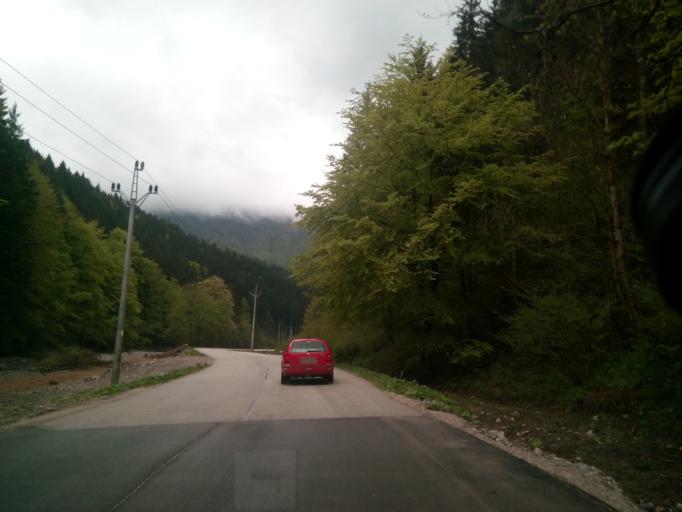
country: SK
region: Zilinsky
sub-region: Okres Zilina
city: Terchova
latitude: 49.2180
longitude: 19.0355
